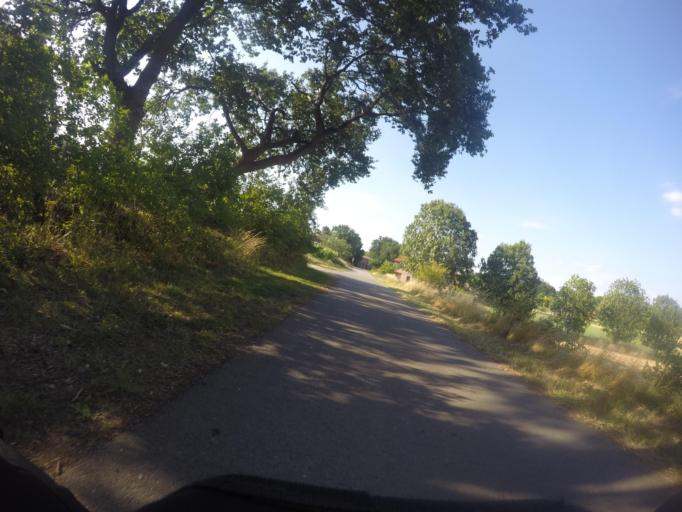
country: DE
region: Lower Saxony
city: Dahlem
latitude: 53.2006
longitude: 10.7439
